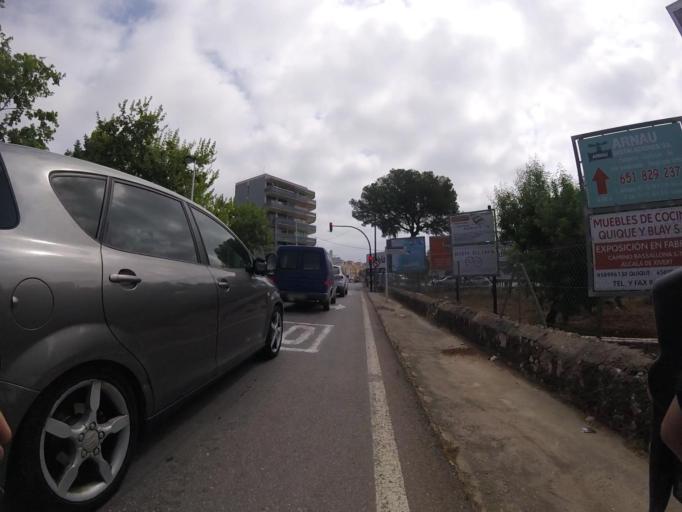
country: ES
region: Valencia
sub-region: Provincia de Castello
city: Alcoceber
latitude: 40.2440
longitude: 0.2726
